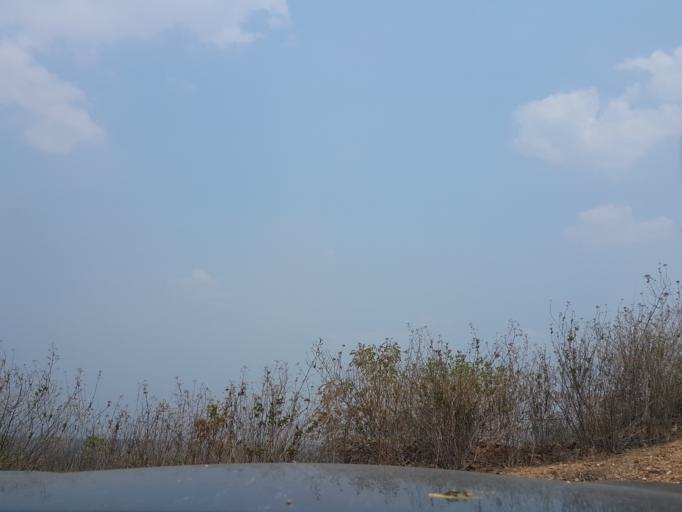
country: TH
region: Lampang
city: Mae Phrik
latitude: 17.4988
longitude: 99.0692
